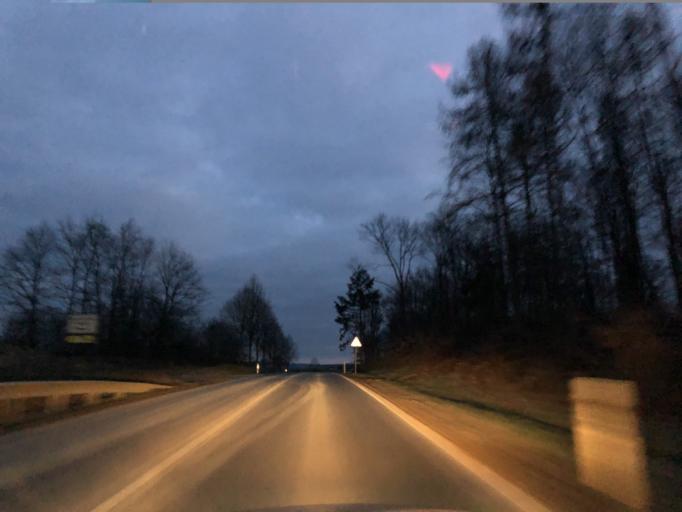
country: DE
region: Rheinland-Pfalz
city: Singhofen
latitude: 50.2880
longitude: 7.8260
